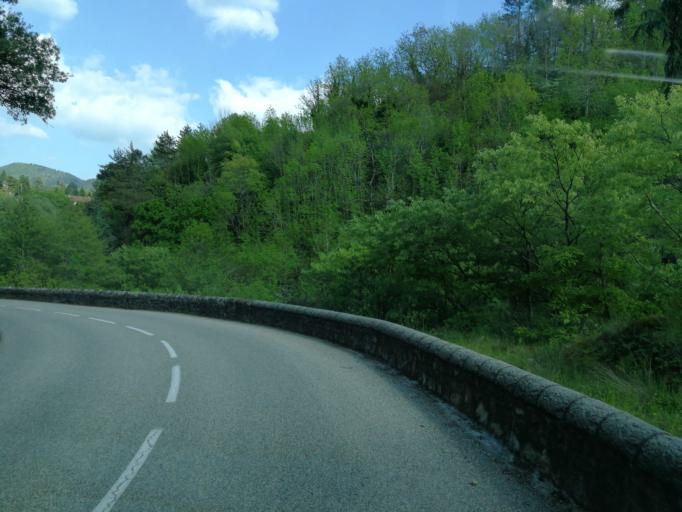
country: FR
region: Rhone-Alpes
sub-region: Departement de l'Ardeche
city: Saint-Sauveur-de-Montagut
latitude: 44.8062
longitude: 4.6096
